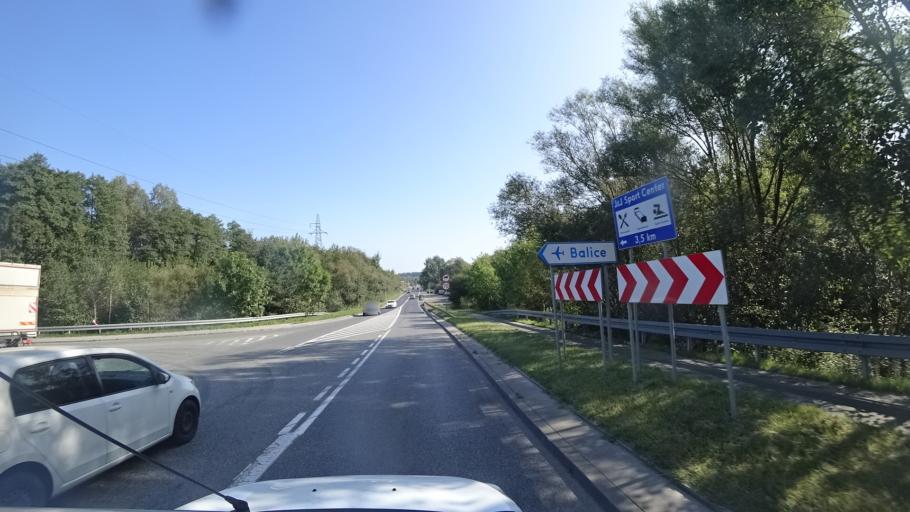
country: PL
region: Lesser Poland Voivodeship
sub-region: Krakow
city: Sidzina
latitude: 49.9977
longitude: 19.8567
